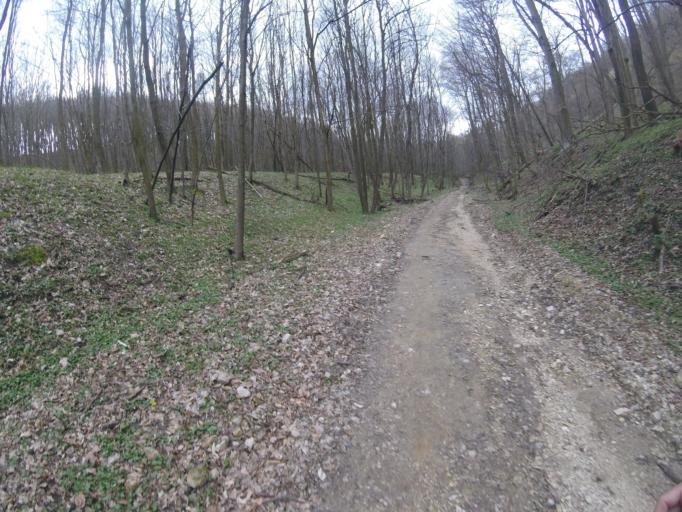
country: HU
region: Fejer
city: Szarliget
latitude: 47.4657
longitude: 18.4489
